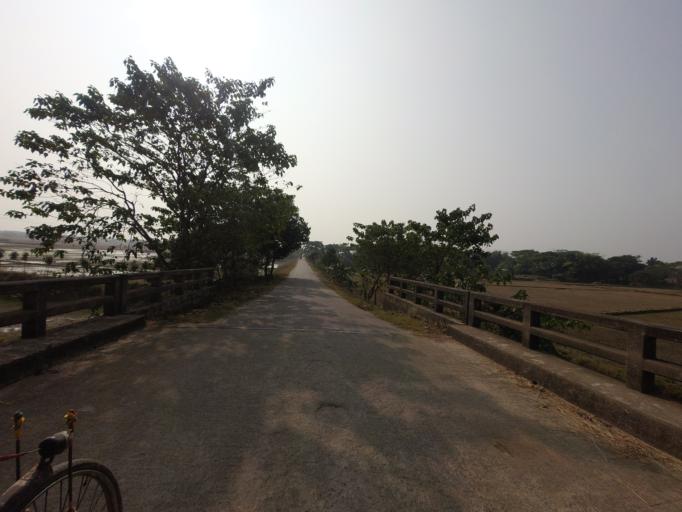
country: BD
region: Dhaka
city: Netrakona
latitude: 25.0258
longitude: 90.6927
